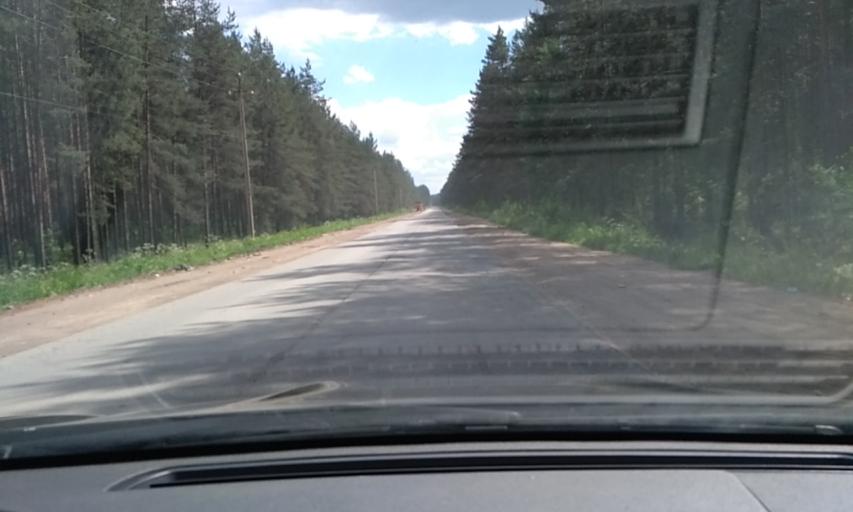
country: RU
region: Leningrad
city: Imeni Sverdlova
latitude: 59.8530
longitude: 30.6772
